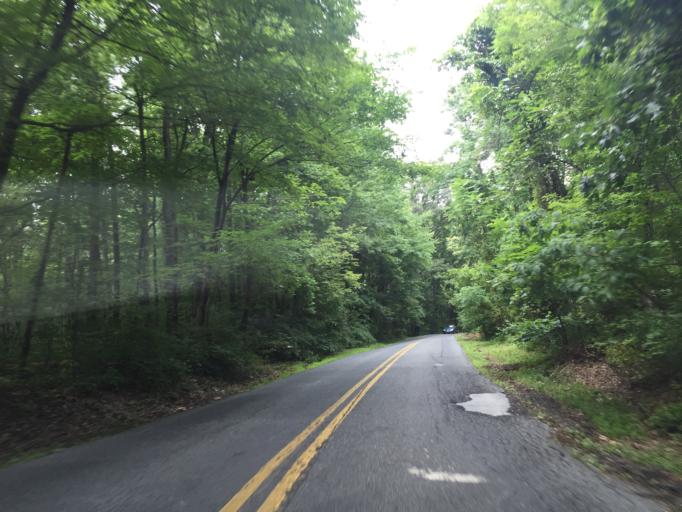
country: US
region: Maryland
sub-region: Baltimore County
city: Edgemere
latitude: 39.2691
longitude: -76.4583
